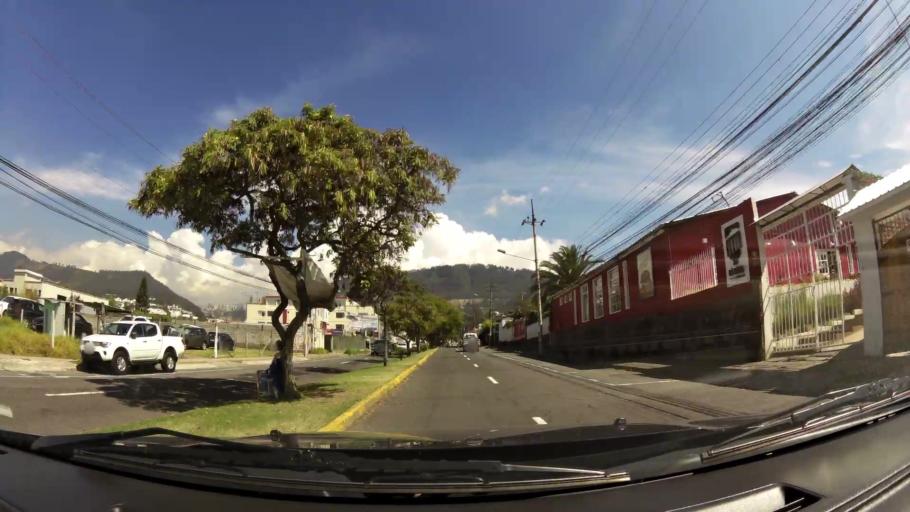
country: EC
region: Pichincha
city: Quito
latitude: -0.1950
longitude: -78.4366
